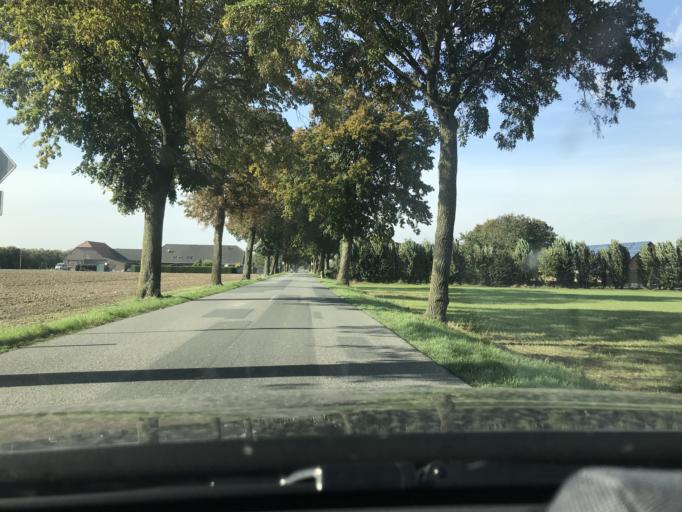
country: DE
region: North Rhine-Westphalia
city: Kalkar
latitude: 51.7172
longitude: 6.2703
